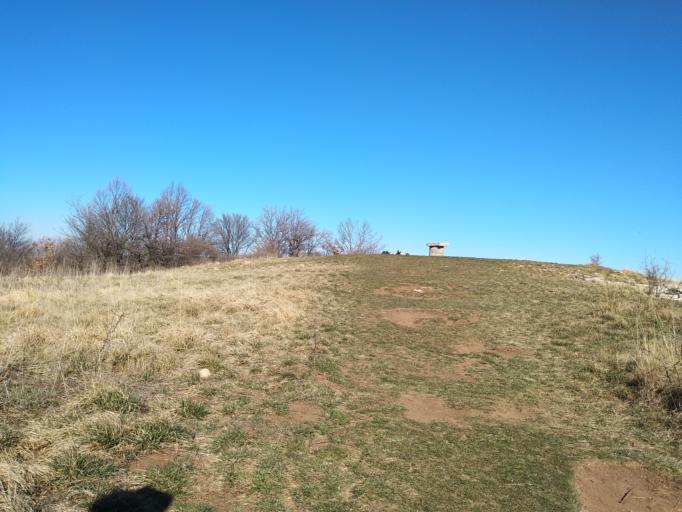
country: IT
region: Emilia-Romagna
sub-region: Provincia di Reggio Emilia
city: Castelnovo ne'Monti
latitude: 44.4208
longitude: 10.4141
